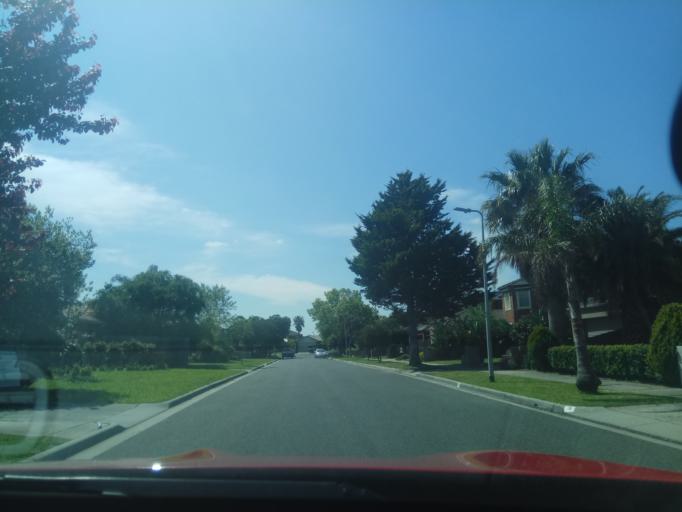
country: AU
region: Victoria
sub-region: Kingston
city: Aspendale Gardens
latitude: -38.0249
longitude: 145.1168
